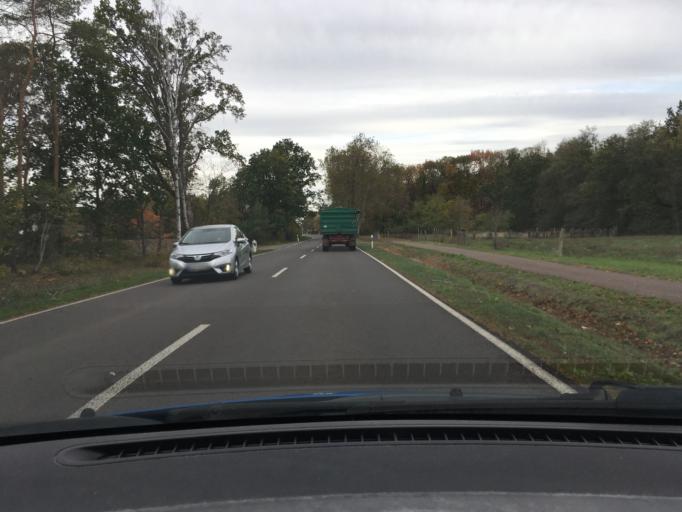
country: DE
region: Saxony-Anhalt
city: Wahlitz
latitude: 52.0997
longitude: 11.7853
